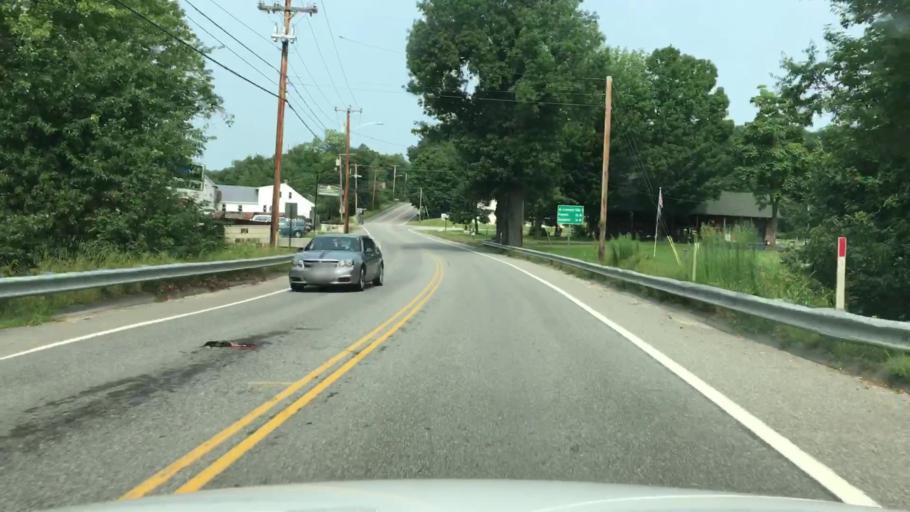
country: US
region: Maine
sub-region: Androscoggin County
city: Livermore Falls
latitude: 44.4619
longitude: -70.1778
